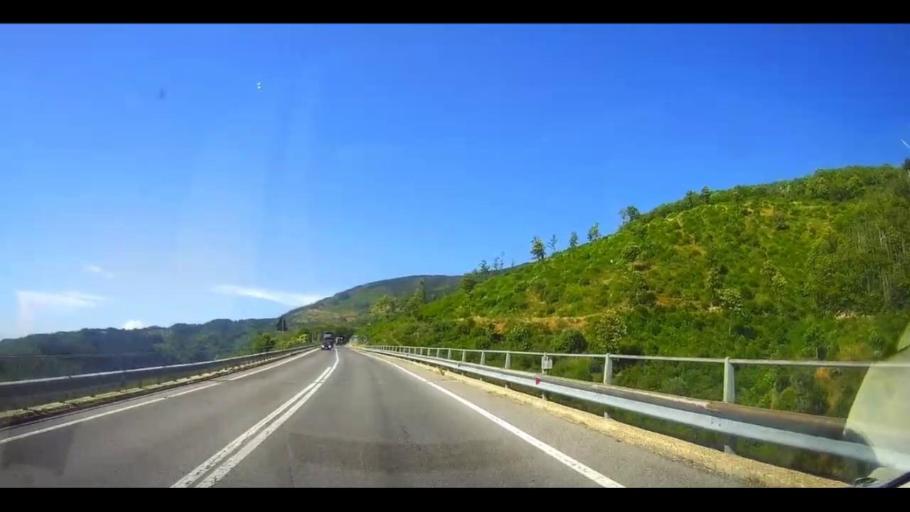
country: IT
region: Calabria
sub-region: Provincia di Cosenza
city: Celico
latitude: 39.3088
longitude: 16.3538
